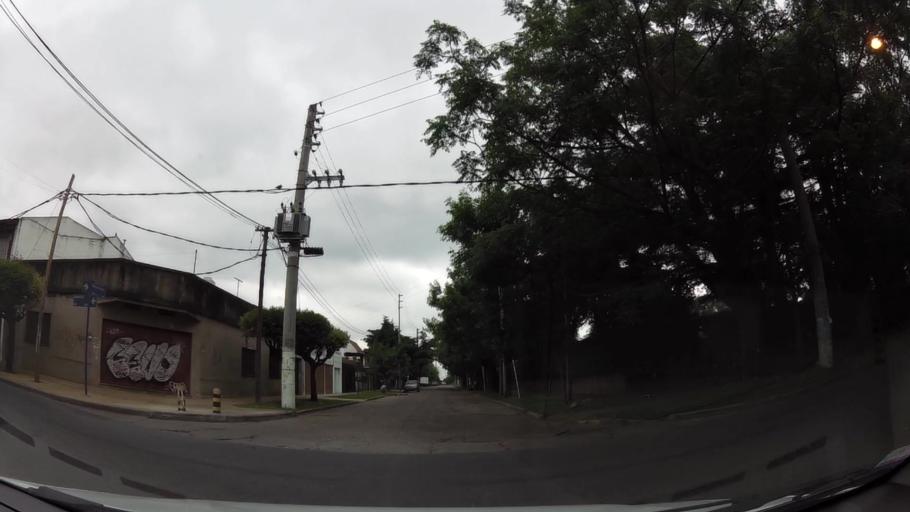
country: AR
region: Buenos Aires F.D.
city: Villa Lugano
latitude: -34.7063
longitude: -58.5125
